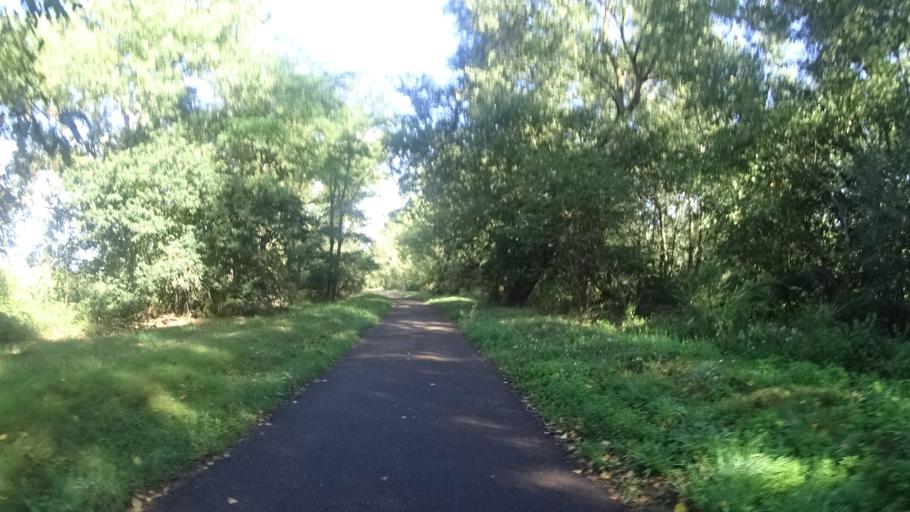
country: FR
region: Bourgogne
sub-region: Departement de la Nievre
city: Pouilly-sur-Loire
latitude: 47.2999
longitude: 2.9188
